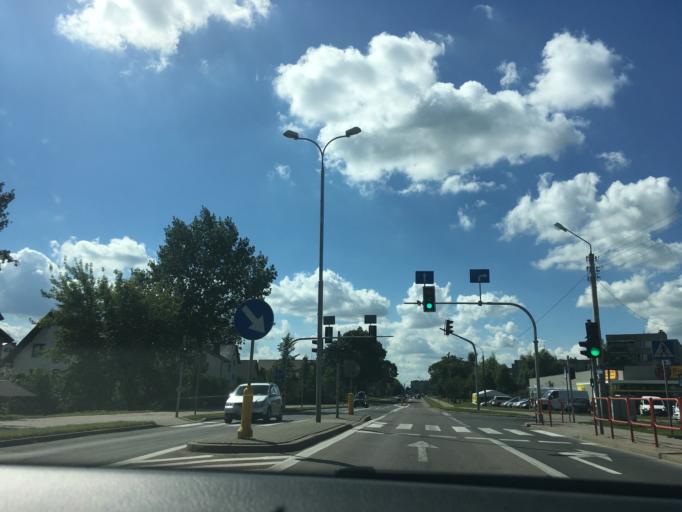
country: PL
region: Podlasie
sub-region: Powiat augustowski
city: Augustow
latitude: 53.8364
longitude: 22.9792
